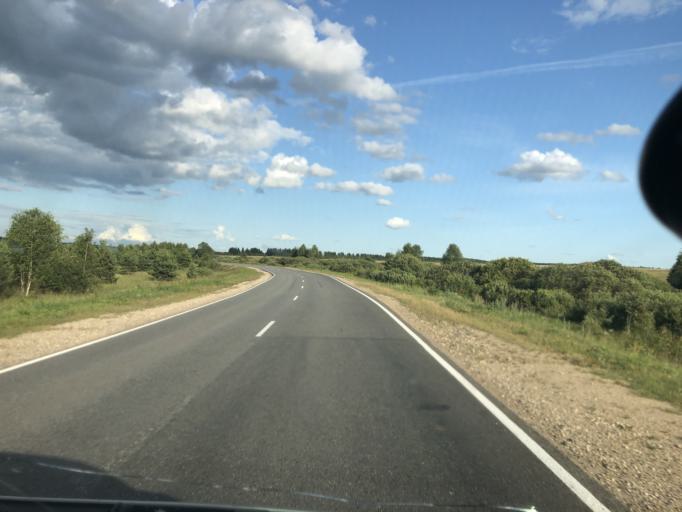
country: RU
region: Kaluga
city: Yukhnov
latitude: 54.7010
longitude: 35.2725
